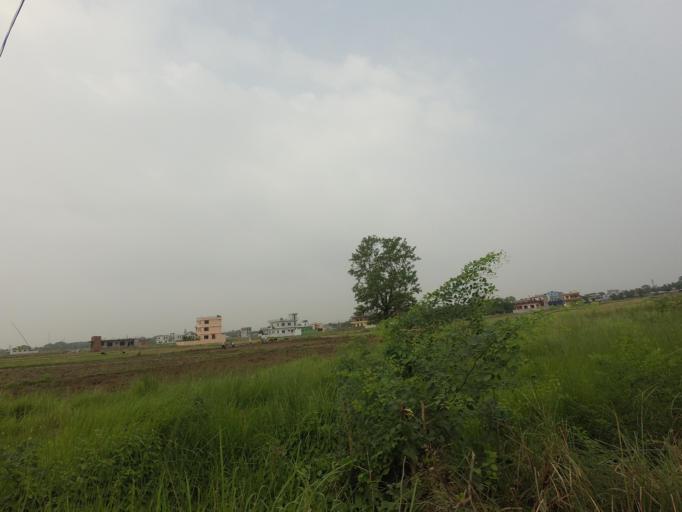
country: NP
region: Western Region
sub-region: Lumbini Zone
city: Bhairahawa
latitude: 27.4896
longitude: 83.4533
